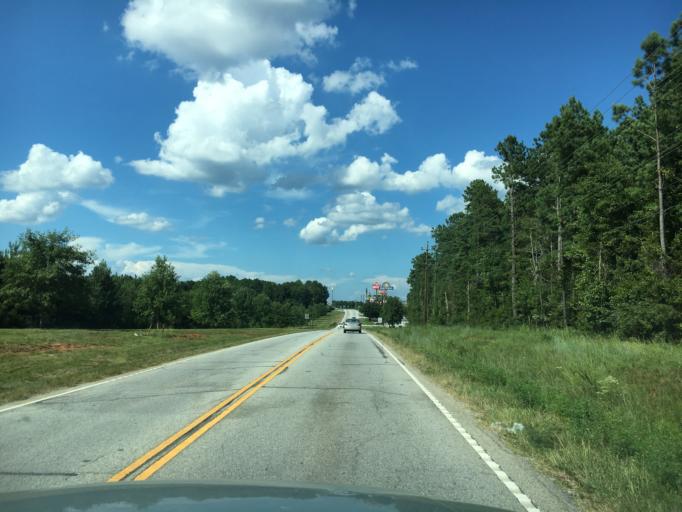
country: US
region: South Carolina
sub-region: Laurens County
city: Clinton
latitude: 34.5002
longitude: -81.8625
